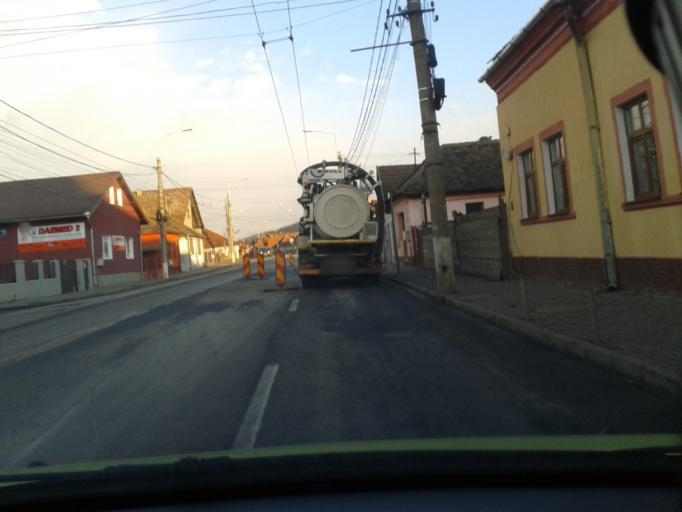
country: RO
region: Sibiu
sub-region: Municipiul Medias
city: Medias
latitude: 46.1654
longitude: 24.3590
